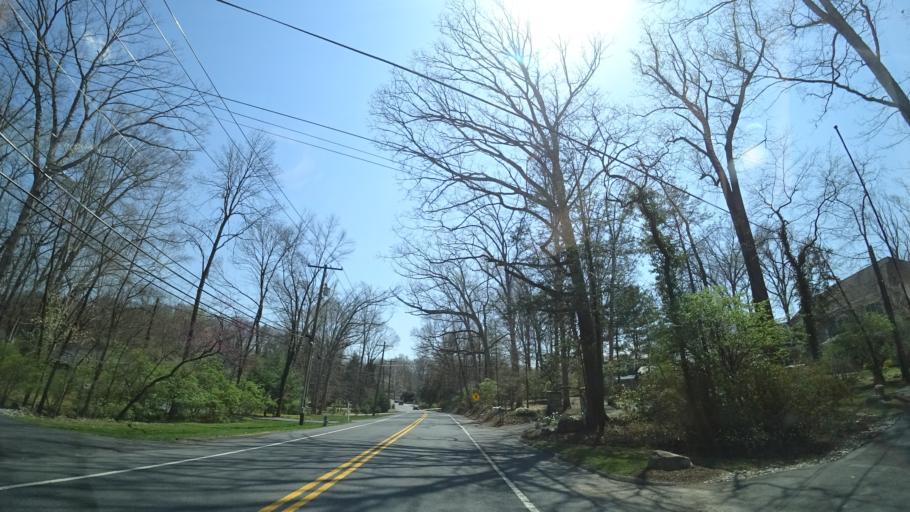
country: US
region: Maryland
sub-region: Montgomery County
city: Cabin John
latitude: 38.9997
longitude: -77.1319
